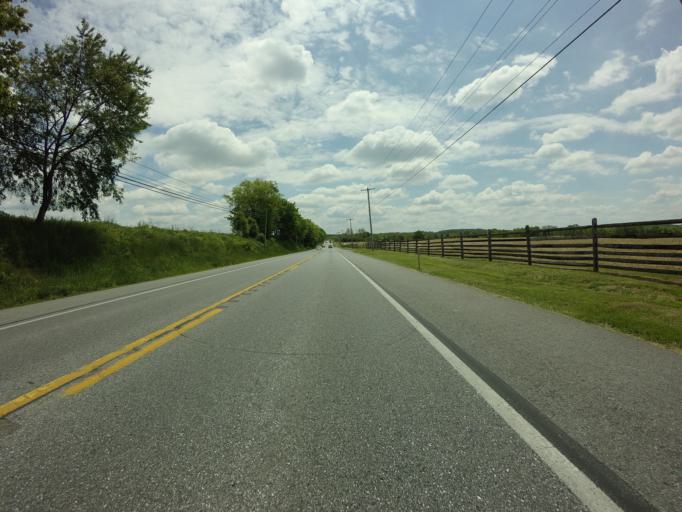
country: US
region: Maryland
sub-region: Frederick County
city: Ballenger Creek
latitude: 39.3740
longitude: -77.3951
